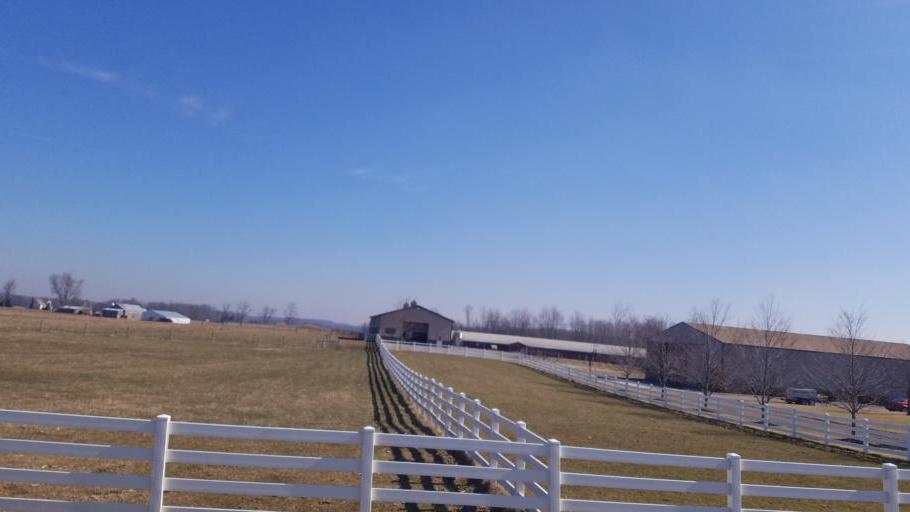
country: US
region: Ohio
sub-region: Richland County
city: Shelby
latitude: 40.8906
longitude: -82.5544
